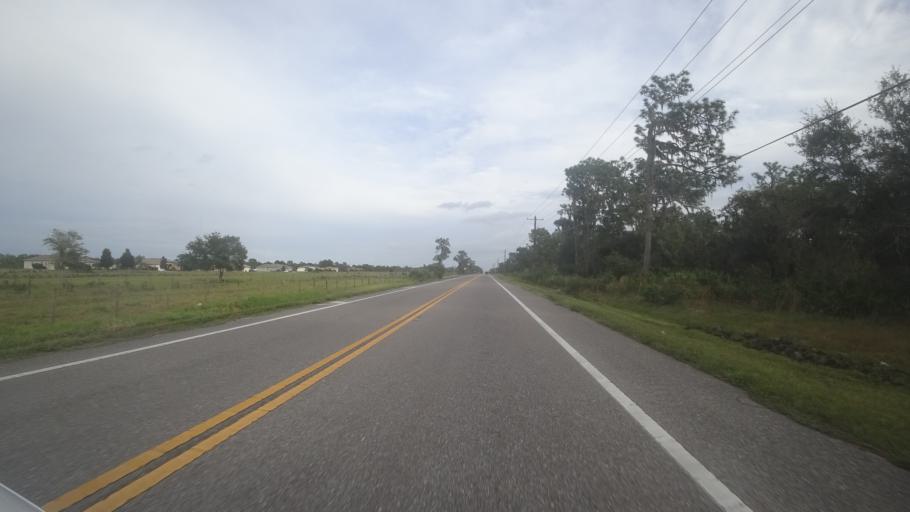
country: US
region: Florida
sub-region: Sarasota County
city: Lake Sarasota
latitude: 27.3870
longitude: -82.2758
